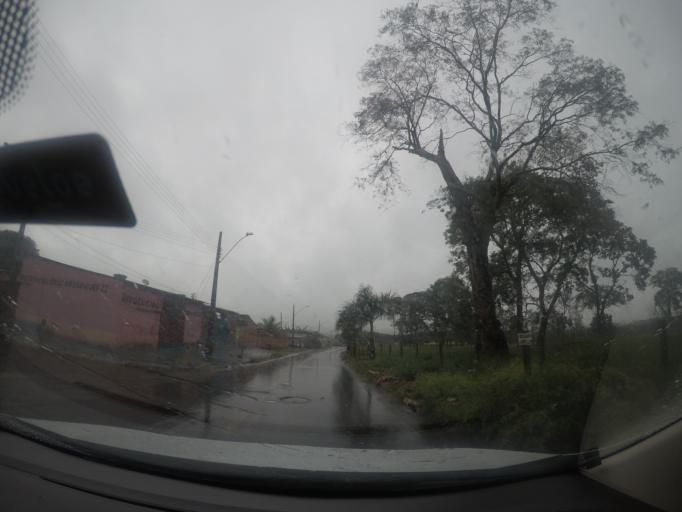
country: BR
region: Goias
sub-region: Goianira
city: Goianira
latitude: -16.5915
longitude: -49.3501
